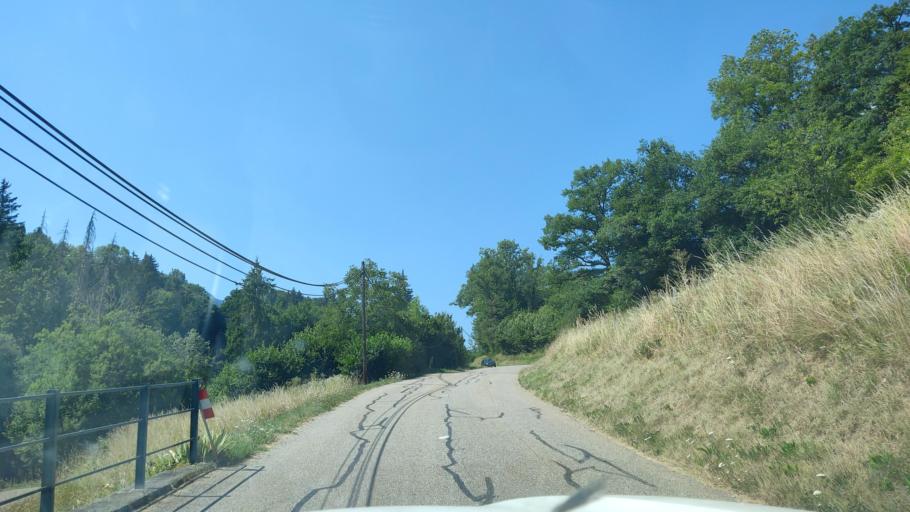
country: FR
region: Rhone-Alpes
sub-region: Departement de la Haute-Savoie
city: Gruffy
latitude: 45.7151
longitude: 6.1027
